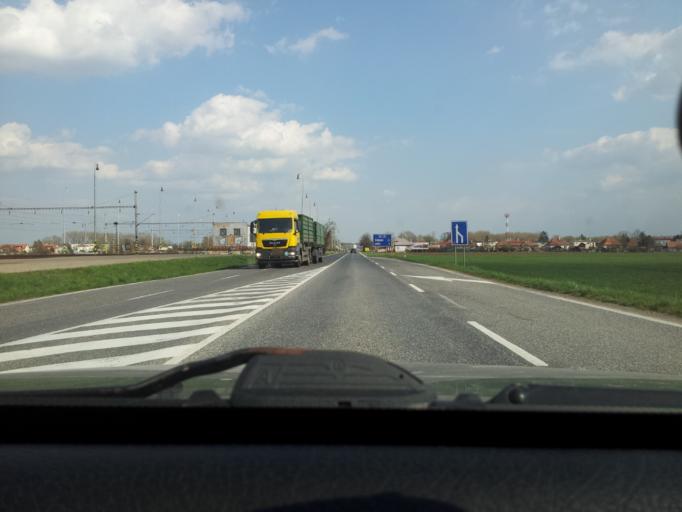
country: SK
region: Nitriansky
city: Tlmace
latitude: 48.2044
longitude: 18.5120
